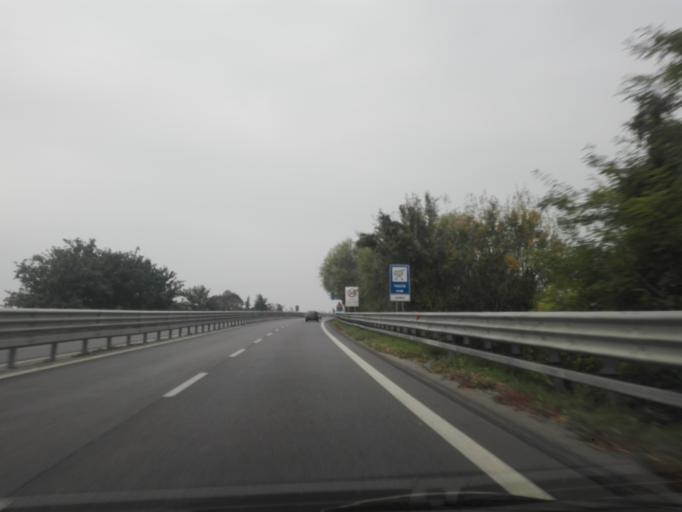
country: IT
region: Veneto
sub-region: Provincia di Verona
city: Legnago
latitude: 45.1812
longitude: 11.2735
